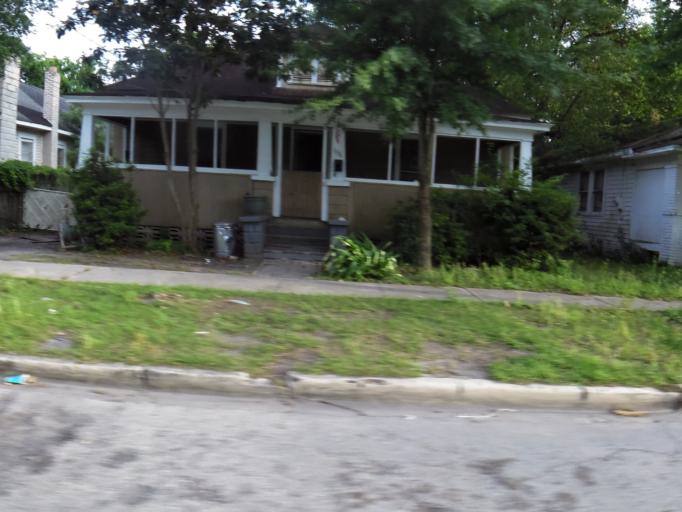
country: US
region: Florida
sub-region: Duval County
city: Jacksonville
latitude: 30.3536
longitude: -81.6403
